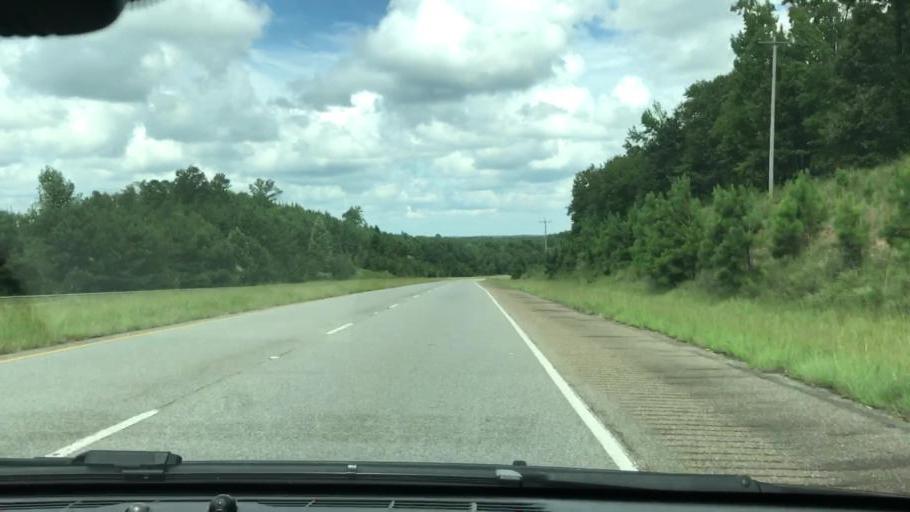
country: US
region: Georgia
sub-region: Stewart County
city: Lumpkin
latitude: 32.1230
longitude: -84.8200
